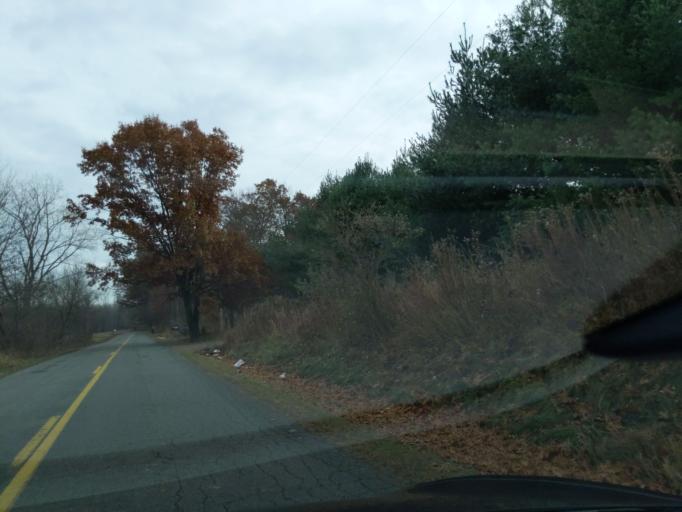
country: US
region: Michigan
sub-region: Ingham County
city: Leslie
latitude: 42.4649
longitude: -84.5127
